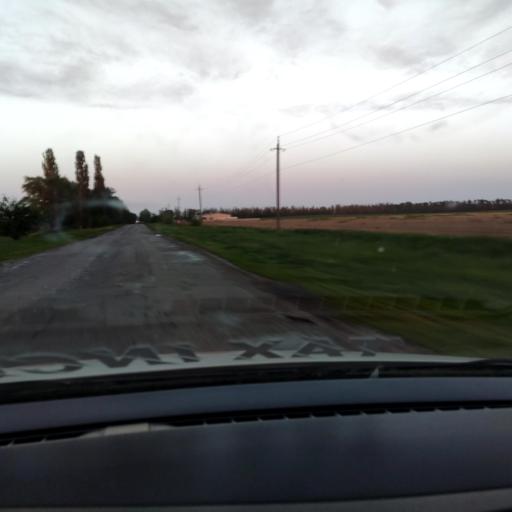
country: RU
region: Voronezj
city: Maslovka
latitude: 51.4455
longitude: 39.2514
